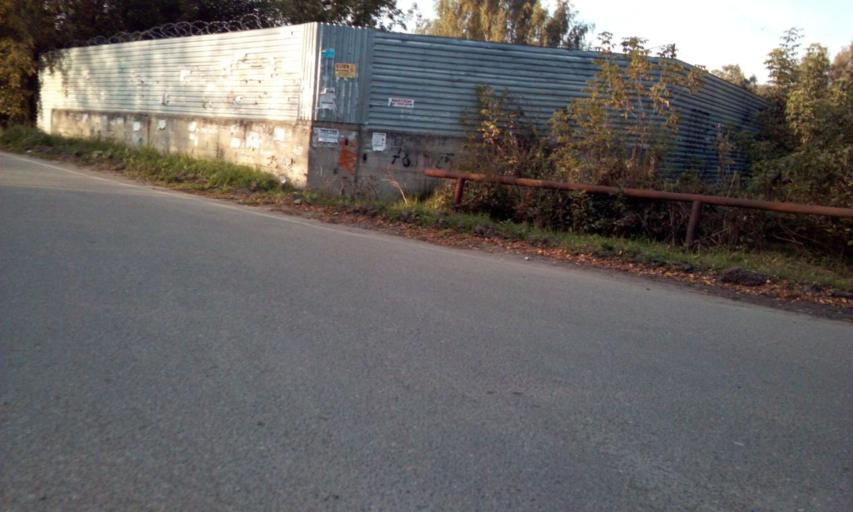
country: RU
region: Moscow
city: Tolstopal'tsevo
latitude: 55.6264
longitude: 37.2232
